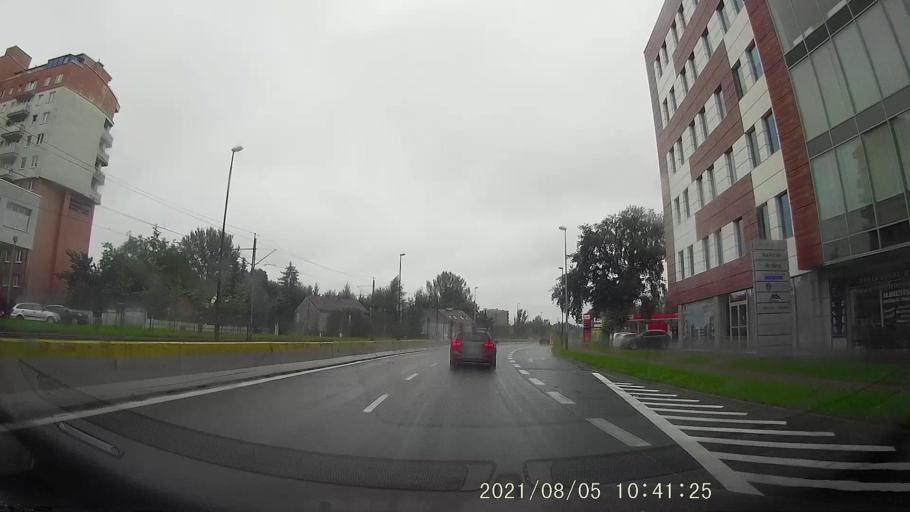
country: PL
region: Lesser Poland Voivodeship
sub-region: Krakow
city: Krakow
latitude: 50.0391
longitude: 19.9253
